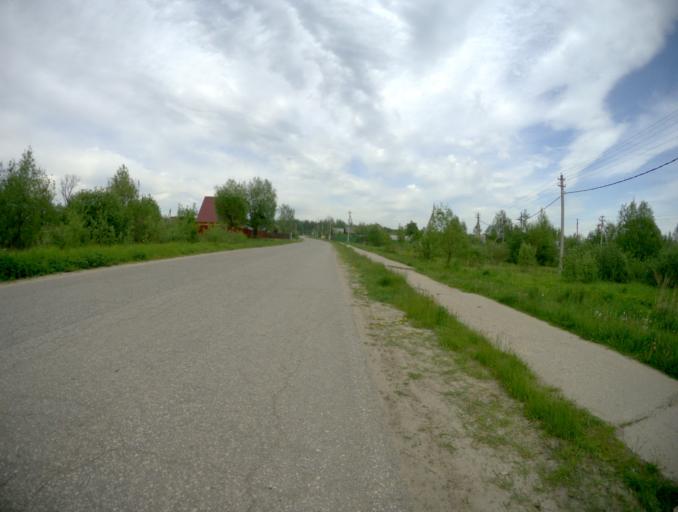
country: RU
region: Vladimir
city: Ivanishchi
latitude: 55.7763
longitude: 40.4256
